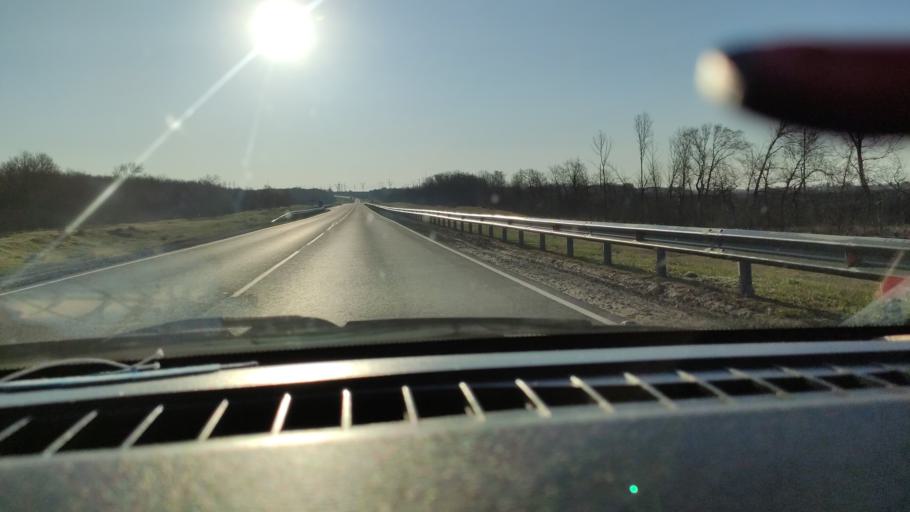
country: RU
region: Saratov
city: Tersa
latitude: 52.0836
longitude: 47.6500
